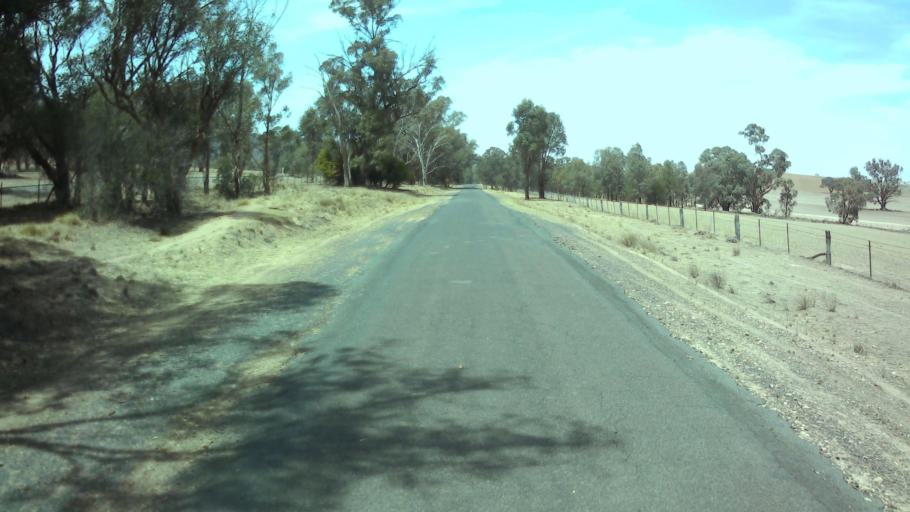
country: AU
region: New South Wales
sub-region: Weddin
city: Grenfell
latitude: -34.0242
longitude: 148.4320
